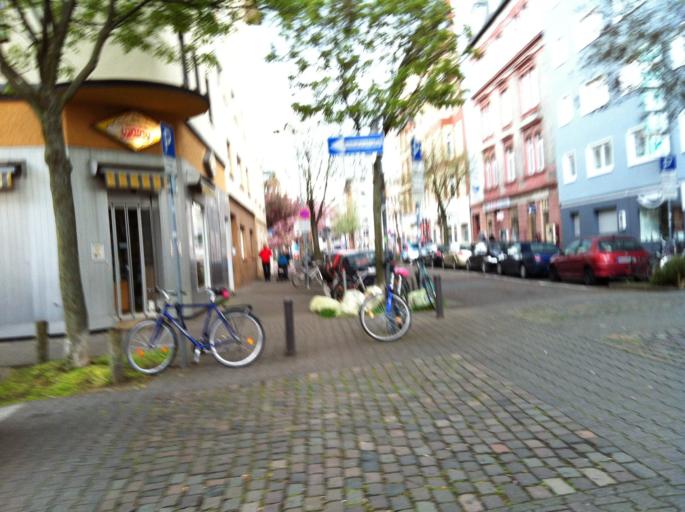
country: DE
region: Rheinland-Pfalz
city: Mainz
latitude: 50.0085
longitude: 8.2615
